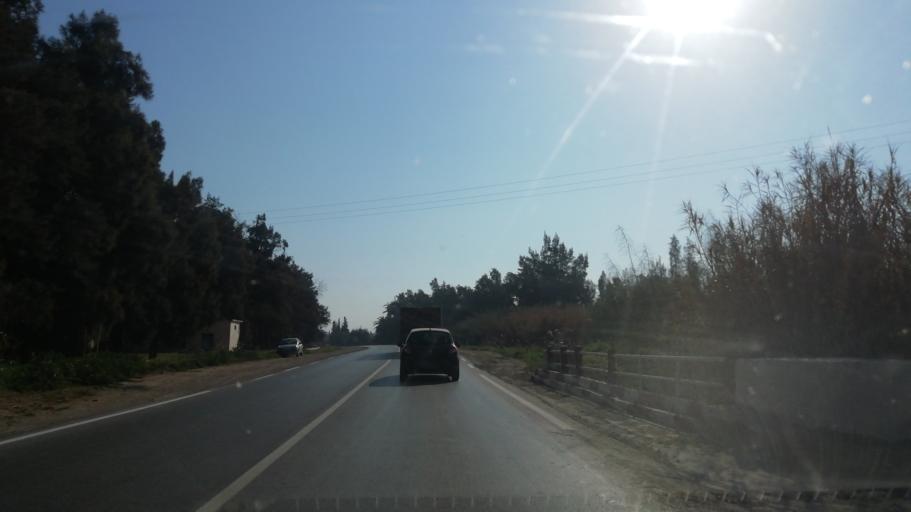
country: DZ
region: Relizane
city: Relizane
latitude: 35.7253
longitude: 0.4806
